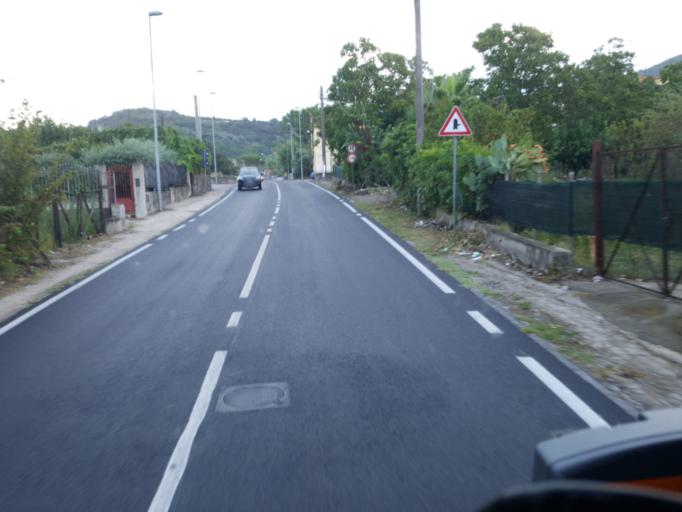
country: IT
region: Campania
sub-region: Provincia di Napoli
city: Carbonara di Nola
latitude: 40.8811
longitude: 14.5694
